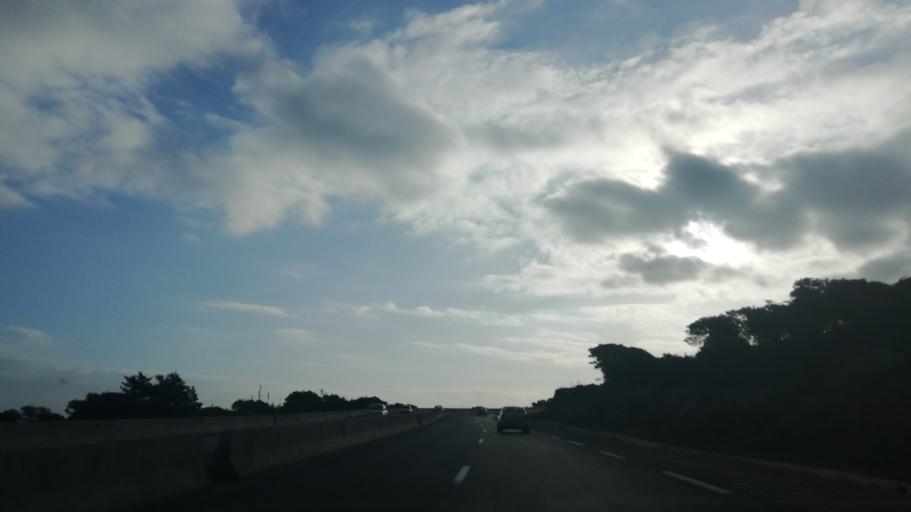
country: DZ
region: Mostaganem
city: Mostaganem
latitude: 36.1123
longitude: 0.2540
